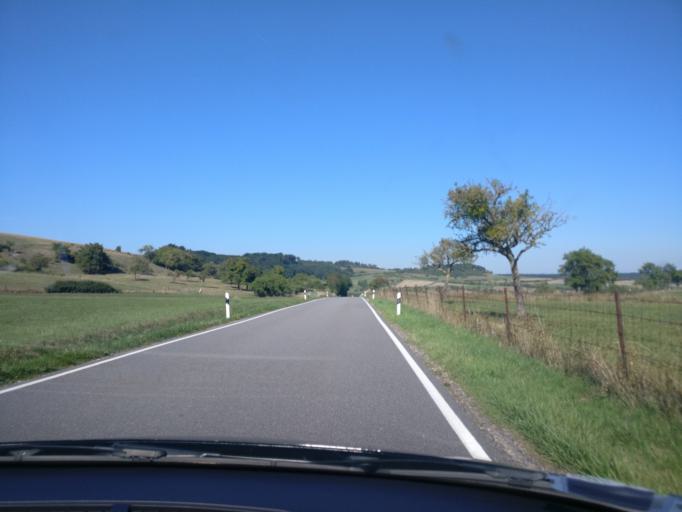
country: LU
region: Grevenmacher
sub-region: Canton d'Echternach
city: Bech
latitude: 49.7444
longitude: 6.3606
